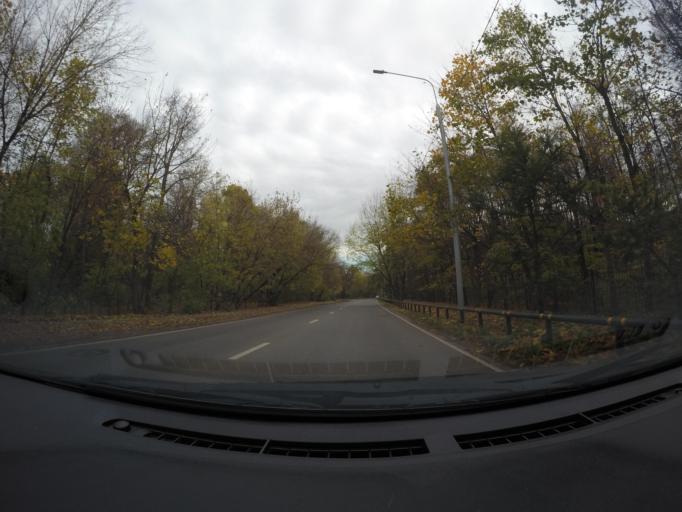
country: RU
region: Moscow
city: Sokol'niki
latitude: 55.8073
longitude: 37.6795
